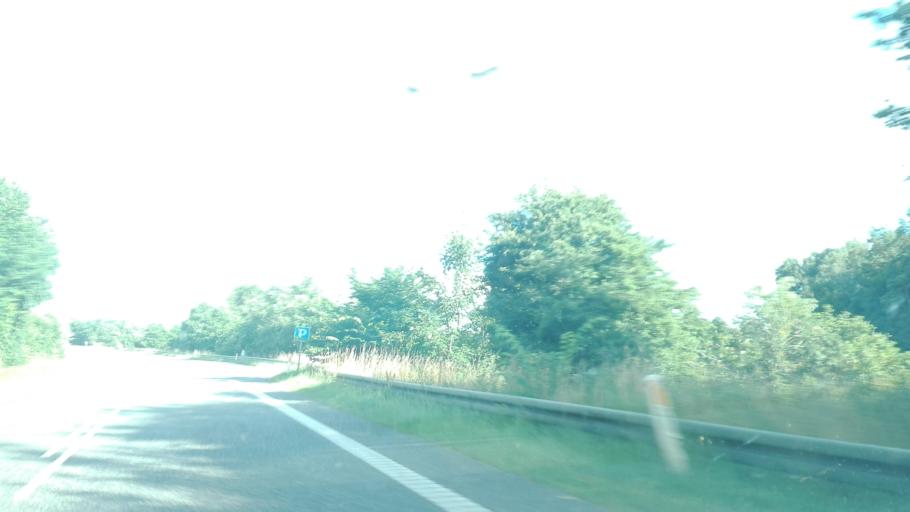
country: DK
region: Central Jutland
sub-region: Skanderborg Kommune
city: Skanderborg
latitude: 56.0467
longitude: 9.8905
